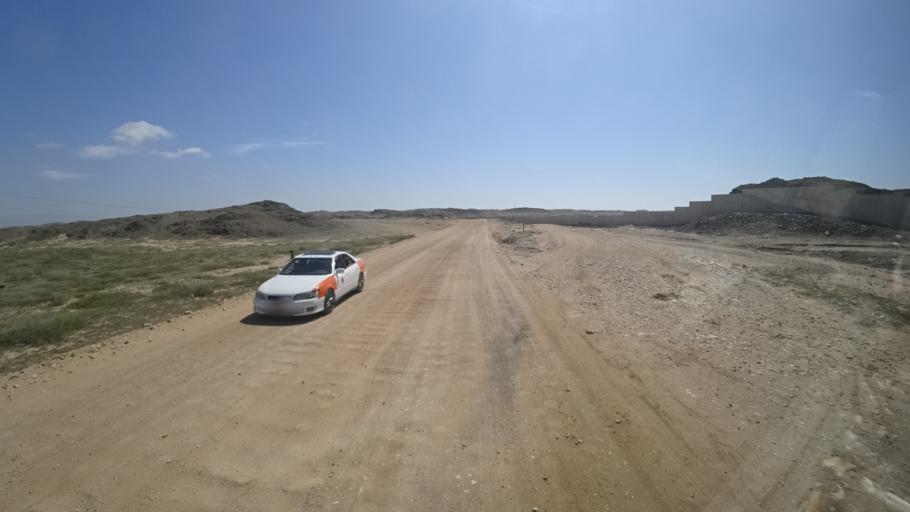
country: OM
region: Zufar
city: Salalah
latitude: 16.9641
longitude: 54.7764
